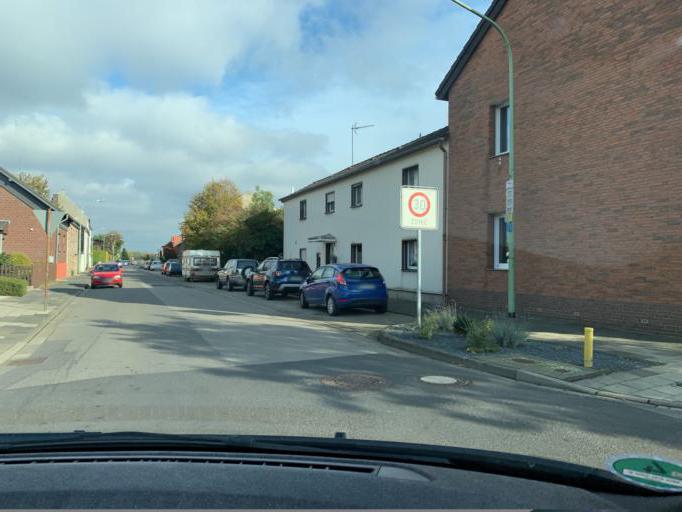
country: DE
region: North Rhine-Westphalia
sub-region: Regierungsbezirk Koln
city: Niederzier
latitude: 50.8667
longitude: 6.4751
